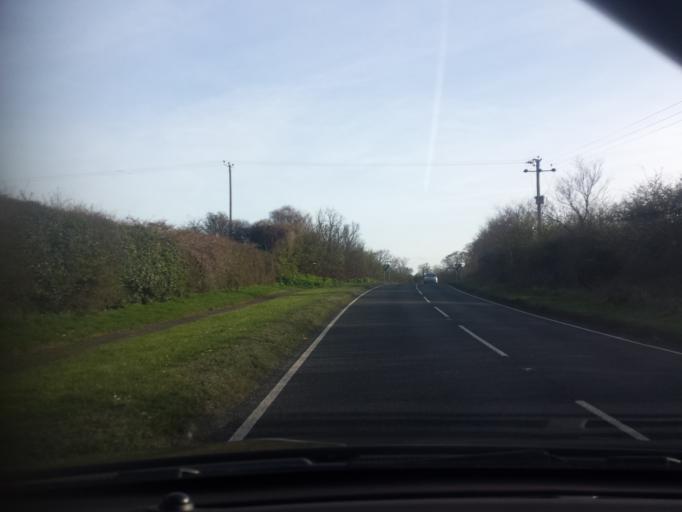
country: GB
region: England
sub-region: Essex
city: Saint Osyth
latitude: 51.8130
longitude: 1.0745
